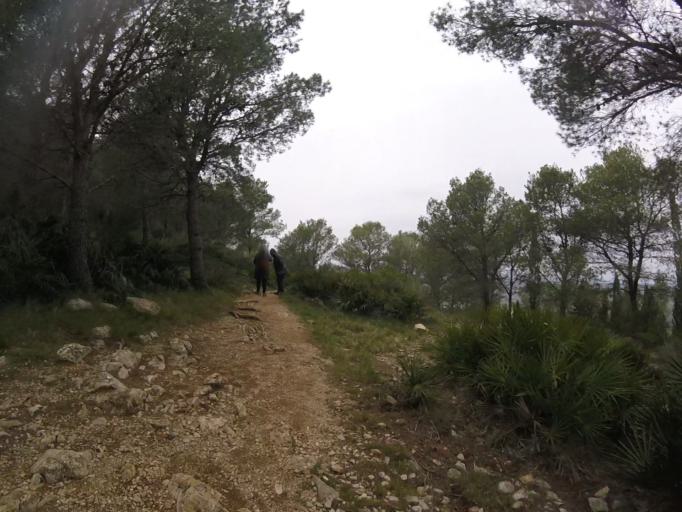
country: ES
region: Valencia
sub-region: Provincia de Castello
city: Alcala de Xivert
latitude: 40.3066
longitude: 0.2552
